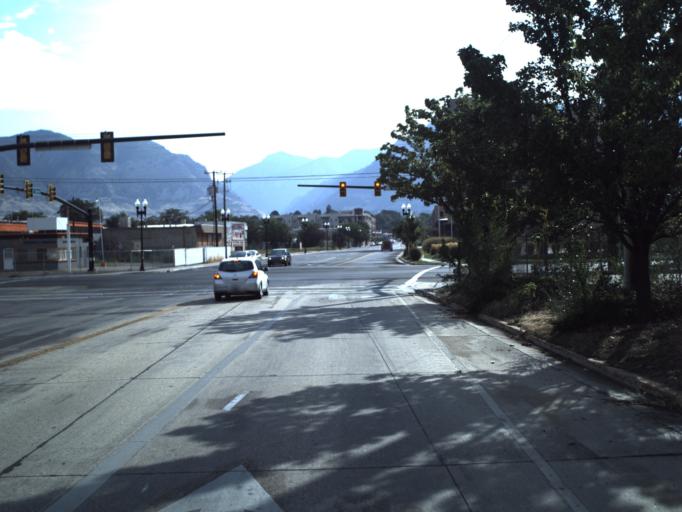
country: US
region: Utah
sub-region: Weber County
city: Ogden
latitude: 41.2311
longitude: -111.9793
